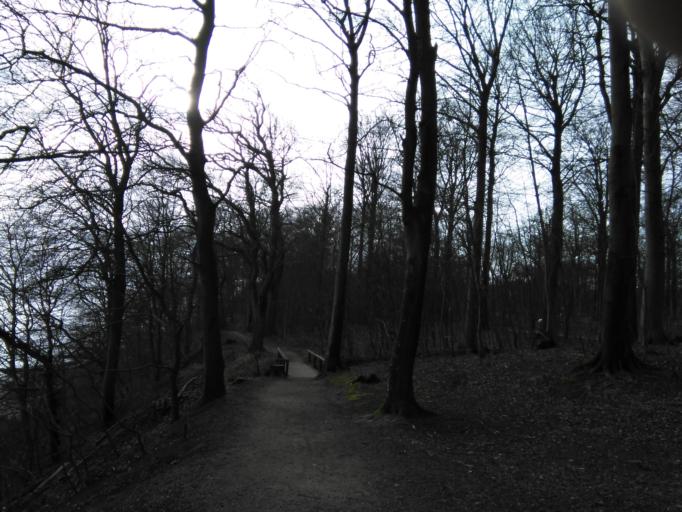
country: DK
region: Central Jutland
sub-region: Arhus Kommune
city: Arhus
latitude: 56.1227
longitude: 10.2210
